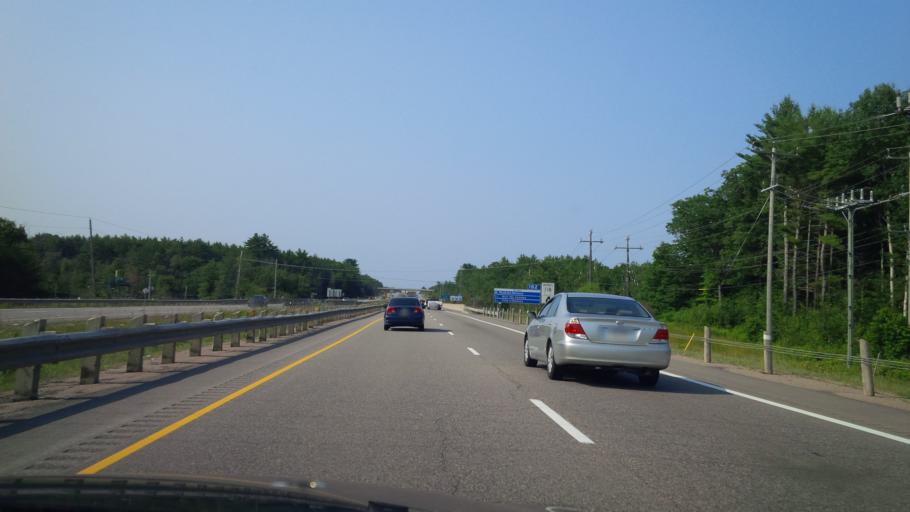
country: CA
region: Ontario
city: Bracebridge
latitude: 45.0039
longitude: -79.3015
